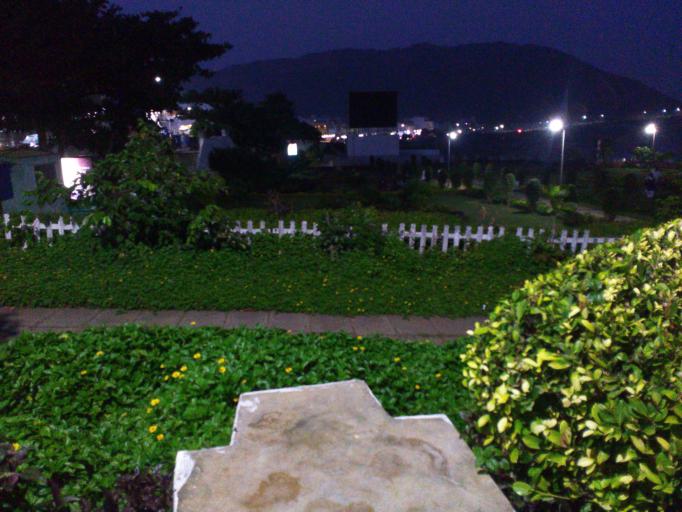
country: IN
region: Andhra Pradesh
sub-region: Vishakhapatnam
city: Yarada
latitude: 17.7482
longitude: 83.3496
